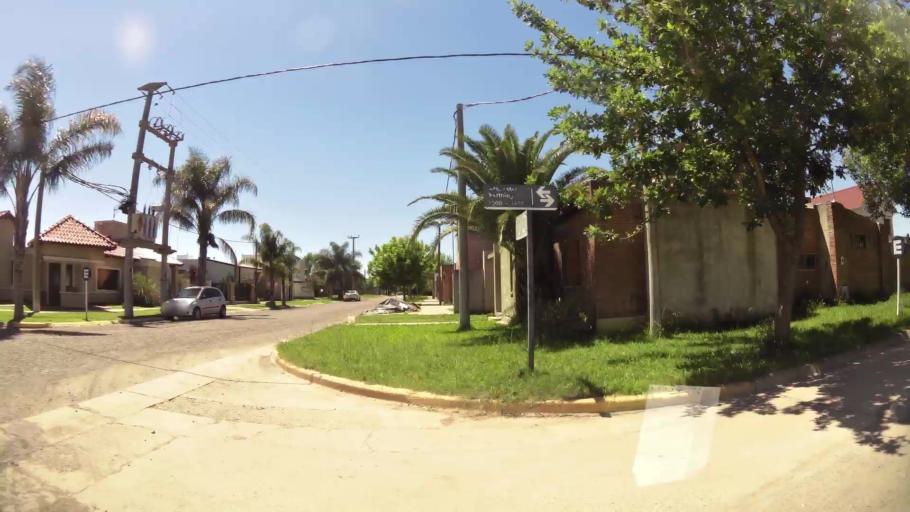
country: AR
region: Santa Fe
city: Esperanza
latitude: -31.3949
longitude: -61.0862
